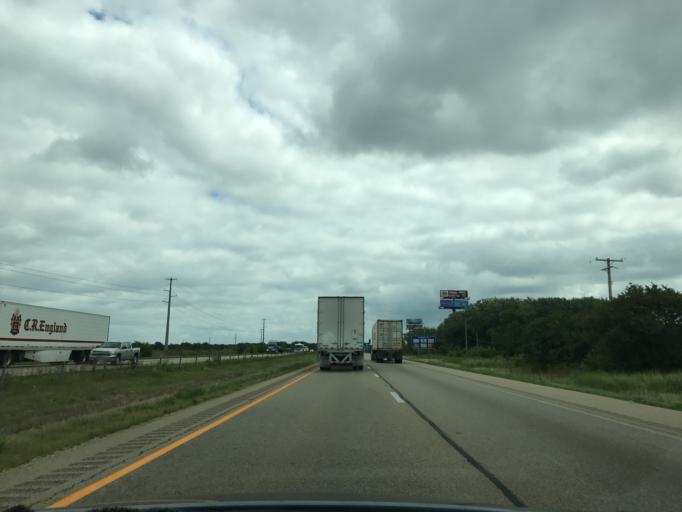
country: US
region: Illinois
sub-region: LaSalle County
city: Ottawa
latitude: 41.3685
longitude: -88.8662
